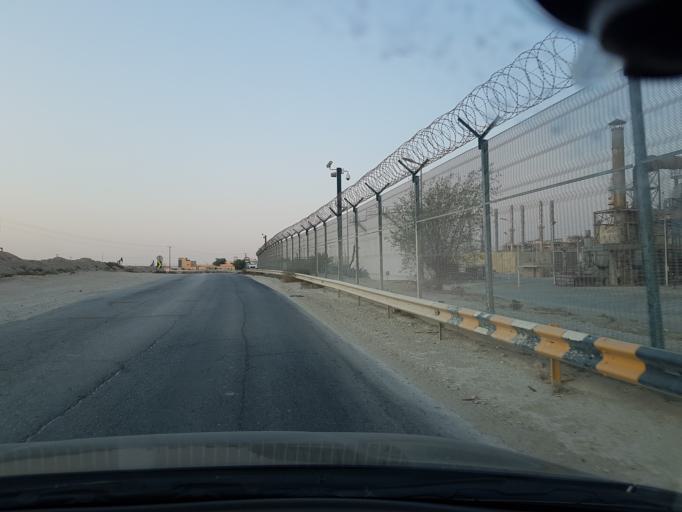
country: BH
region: Central Governorate
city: Dar Kulayb
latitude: 26.0371
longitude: 50.5522
